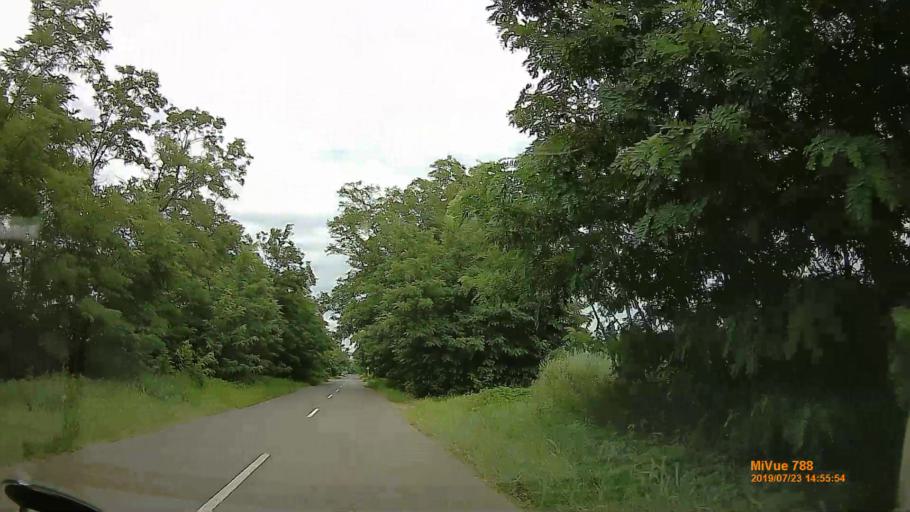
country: HU
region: Szabolcs-Szatmar-Bereg
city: Kalmanhaza
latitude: 47.8949
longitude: 21.6619
